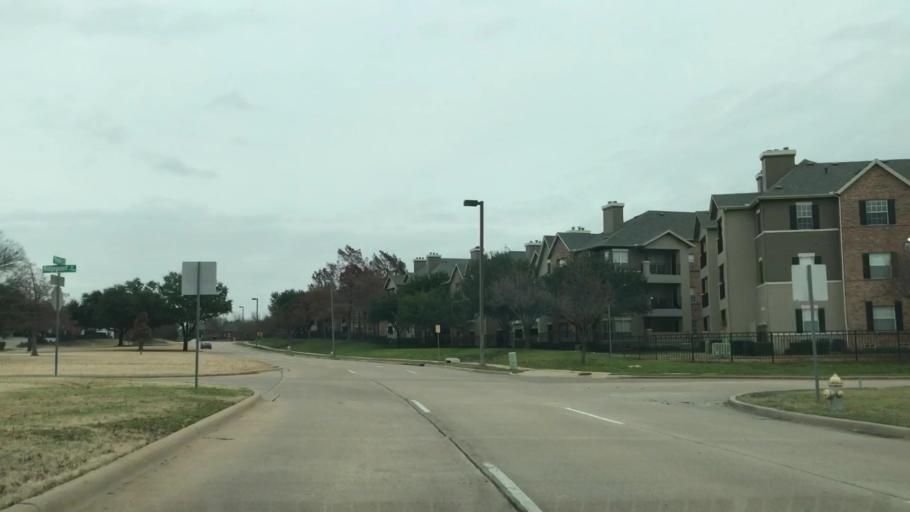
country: US
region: Texas
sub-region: Dallas County
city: Coppell
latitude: 32.9105
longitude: -96.9878
